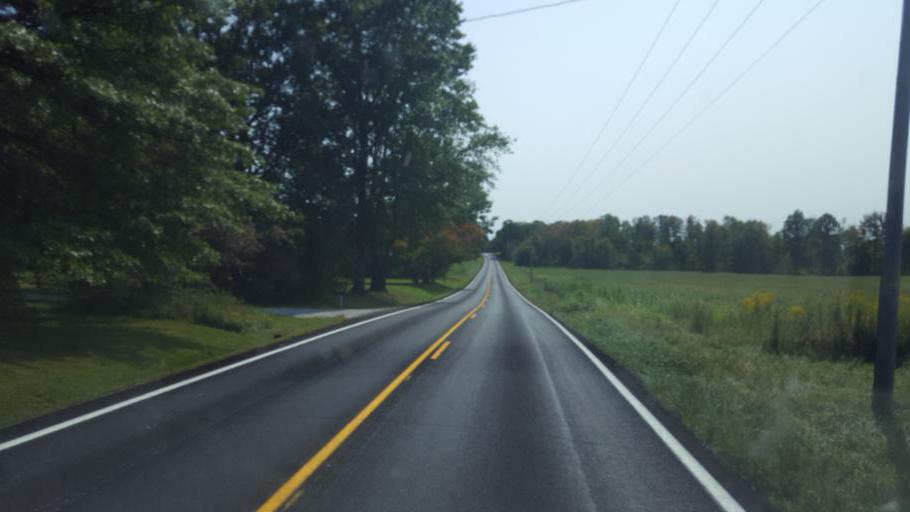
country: US
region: Ohio
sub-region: Sandusky County
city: Bellville
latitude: 40.5772
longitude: -82.5725
